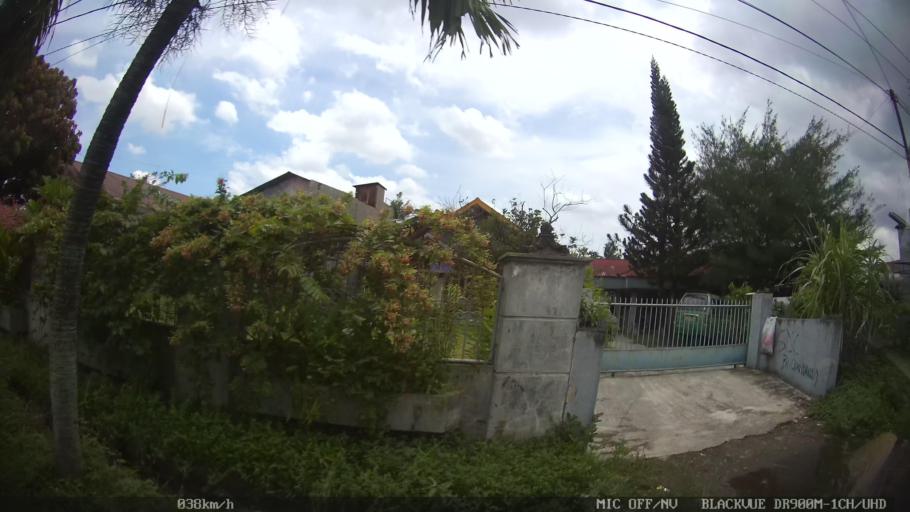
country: ID
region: North Sumatra
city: Medan
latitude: 3.6144
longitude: 98.6493
